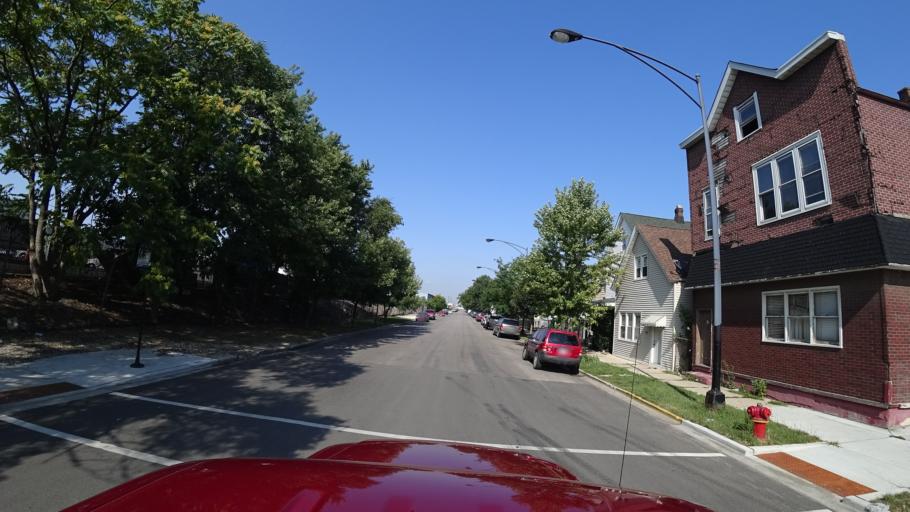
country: US
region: Illinois
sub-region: Cook County
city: Cicero
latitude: 41.8226
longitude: -87.7069
